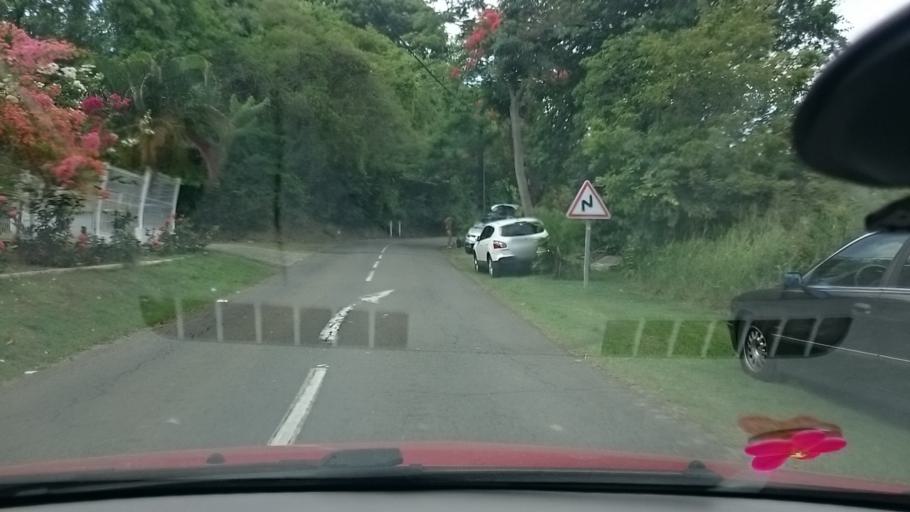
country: MQ
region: Martinique
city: Petite Riviere Salee
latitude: 14.7574
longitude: -60.9219
